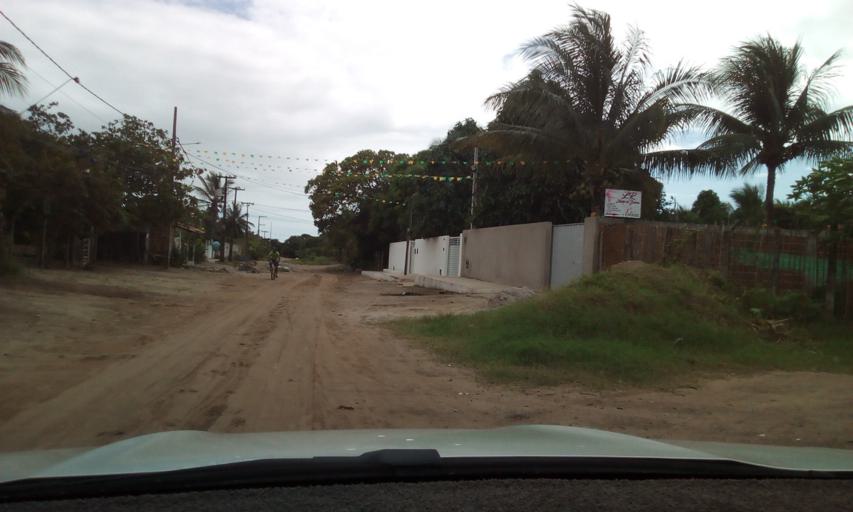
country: BR
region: Paraiba
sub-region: Joao Pessoa
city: Joao Pessoa
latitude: -7.1496
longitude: -34.8063
